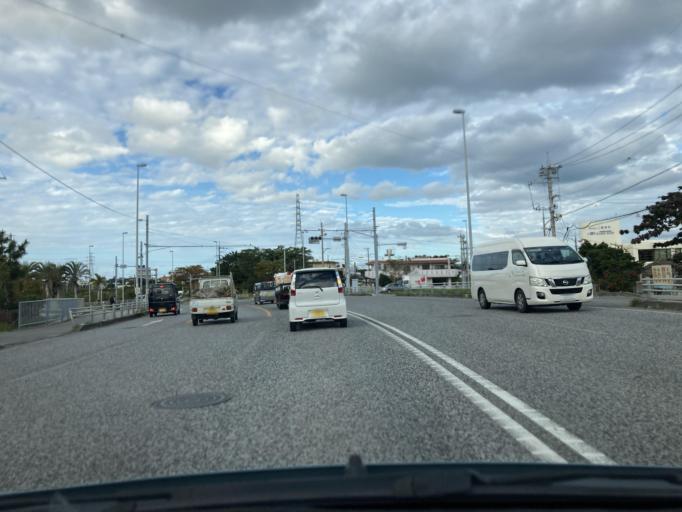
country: JP
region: Okinawa
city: Ishikawa
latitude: 26.3875
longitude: 127.8285
